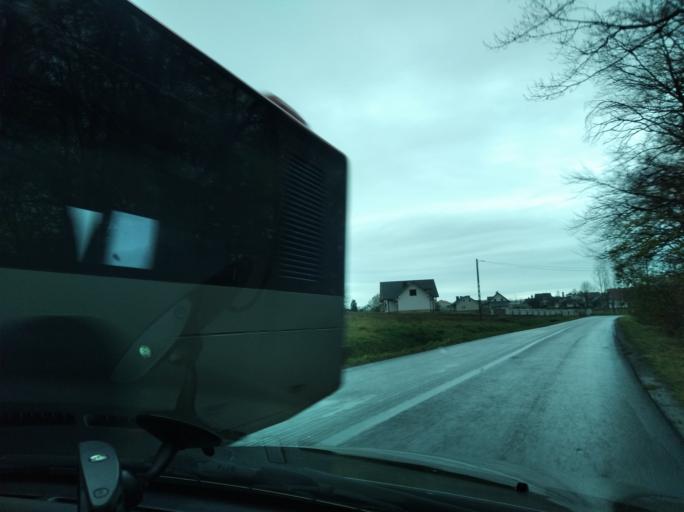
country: PL
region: Subcarpathian Voivodeship
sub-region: Powiat rzeszowski
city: Tyczyn
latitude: 49.9206
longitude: 22.0307
